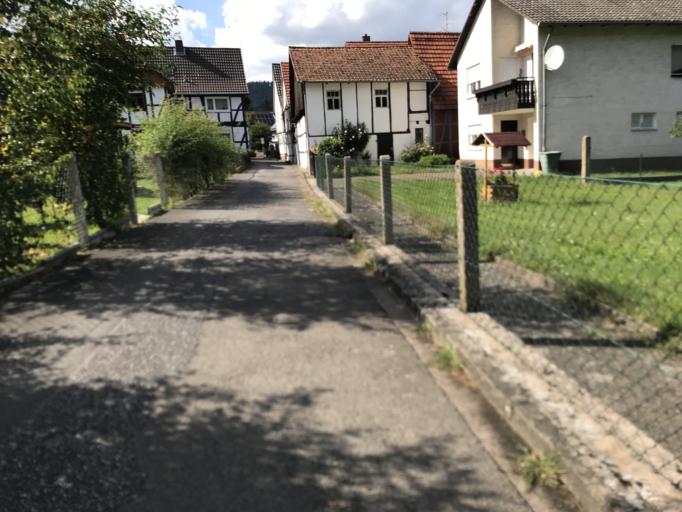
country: DE
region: Hesse
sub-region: Regierungsbezirk Kassel
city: Bad Sooden-Allendorf
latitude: 51.2295
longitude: 9.9986
